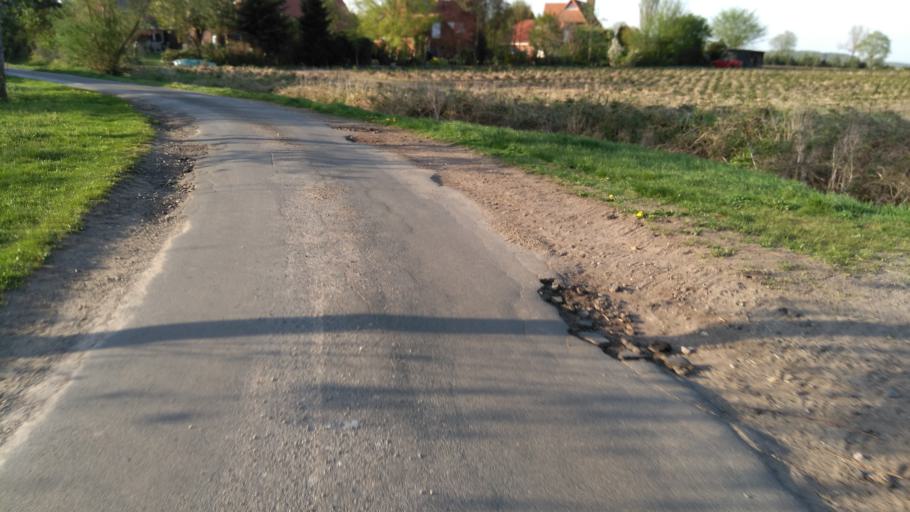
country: DE
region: Lower Saxony
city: Bliedersdorf
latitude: 53.4530
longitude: 9.5681
